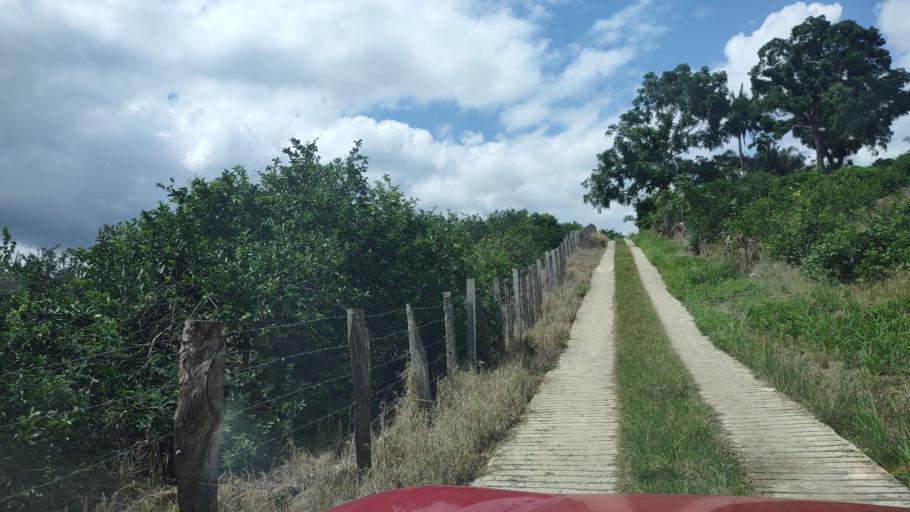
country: MX
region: Puebla
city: San Jose Acateno
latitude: 20.2220
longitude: -97.1496
